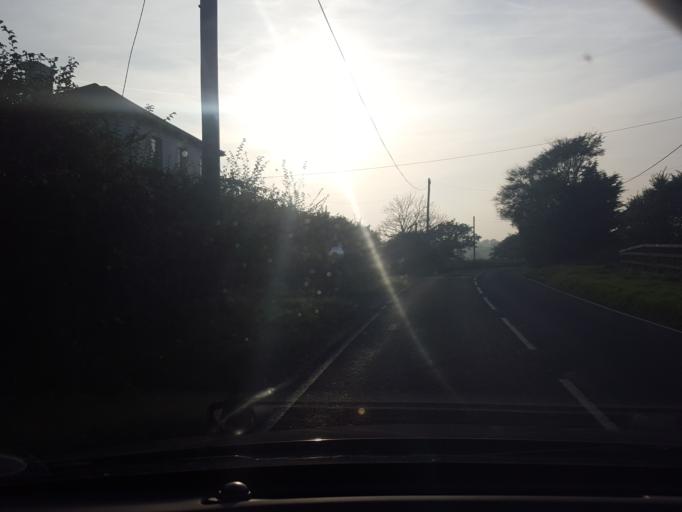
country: GB
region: England
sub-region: Essex
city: Frinton-on-Sea
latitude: 51.8243
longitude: 1.1939
